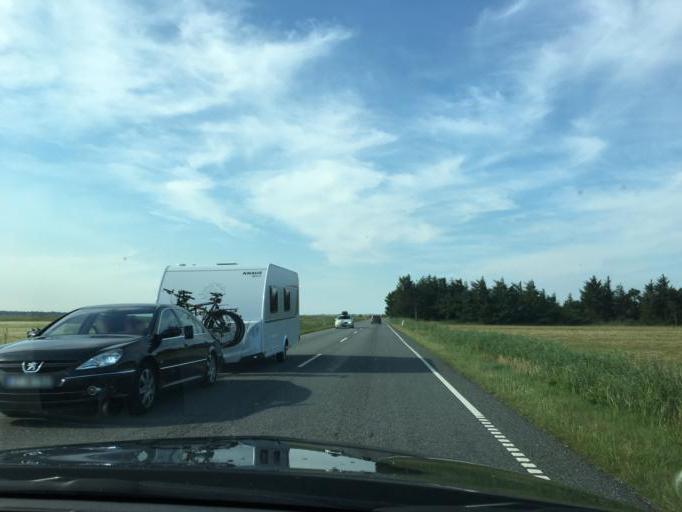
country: DK
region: Central Jutland
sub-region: Ringkobing-Skjern Kommune
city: Hvide Sande
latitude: 55.8546
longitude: 8.1779
